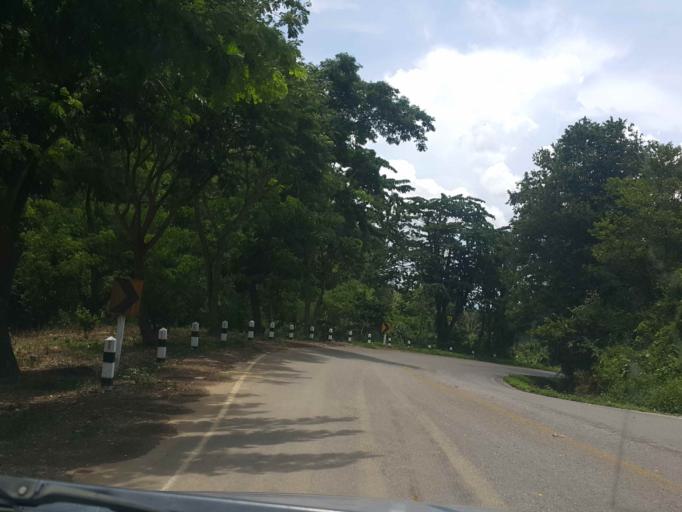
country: TH
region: Phayao
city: Chiang Muan
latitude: 18.9084
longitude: 100.1179
